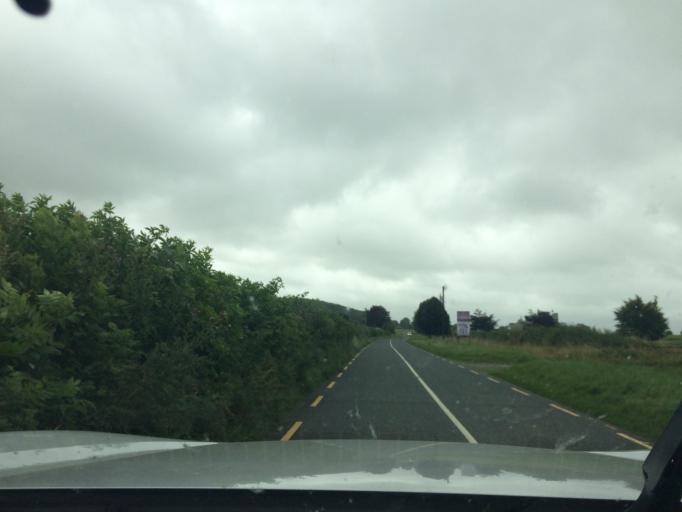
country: IE
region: Munster
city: Cashel
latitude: 52.5314
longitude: -7.8899
